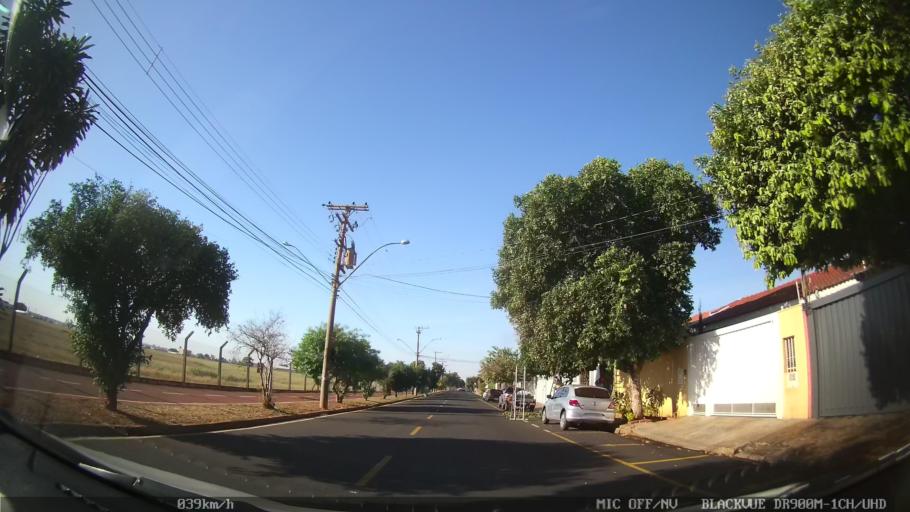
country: BR
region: Sao Paulo
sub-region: Sao Jose Do Rio Preto
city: Sao Jose do Rio Preto
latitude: -20.8157
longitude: -49.4025
